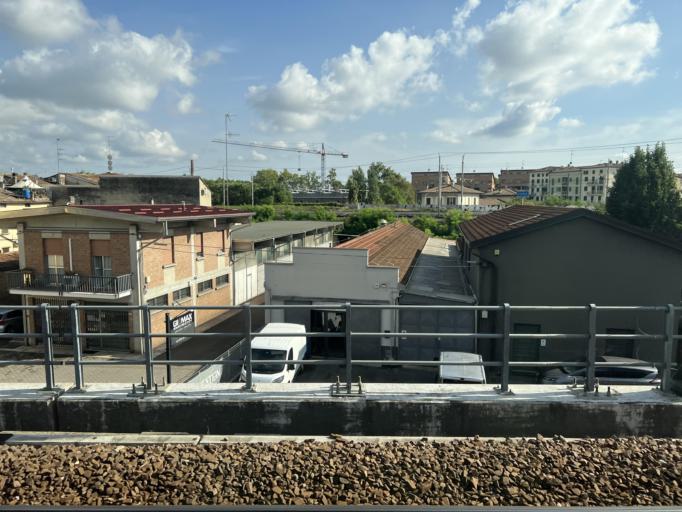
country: IT
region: Emilia-Romagna
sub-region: Provincia di Parma
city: Parma
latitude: 44.8071
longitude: 10.3410
